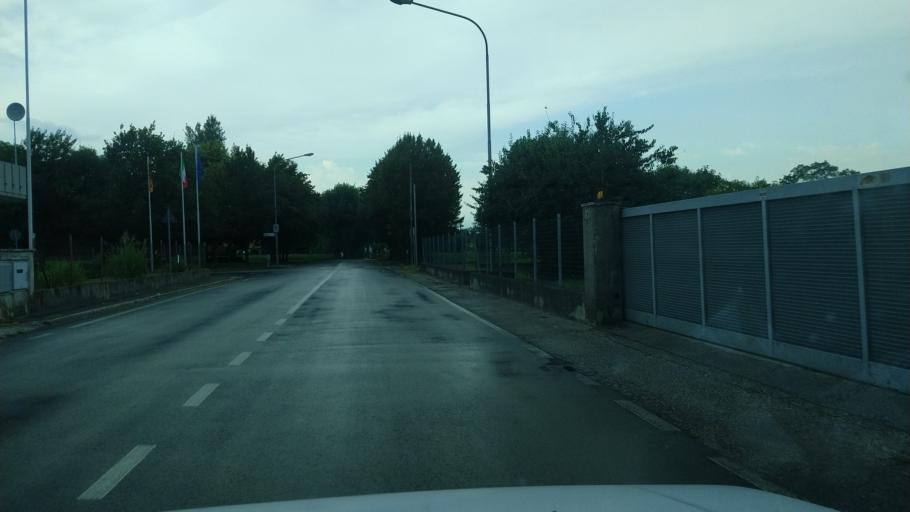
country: IT
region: Veneto
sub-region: Provincia di Vicenza
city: Nove
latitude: 45.7113
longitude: 11.6722
